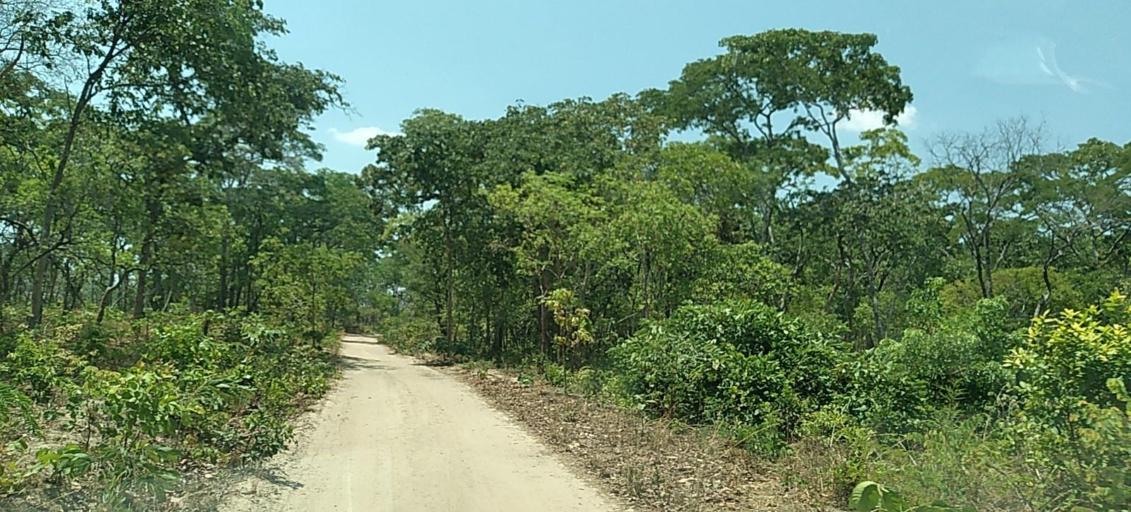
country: ZM
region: Copperbelt
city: Mpongwe
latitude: -13.6404
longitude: 28.4831
